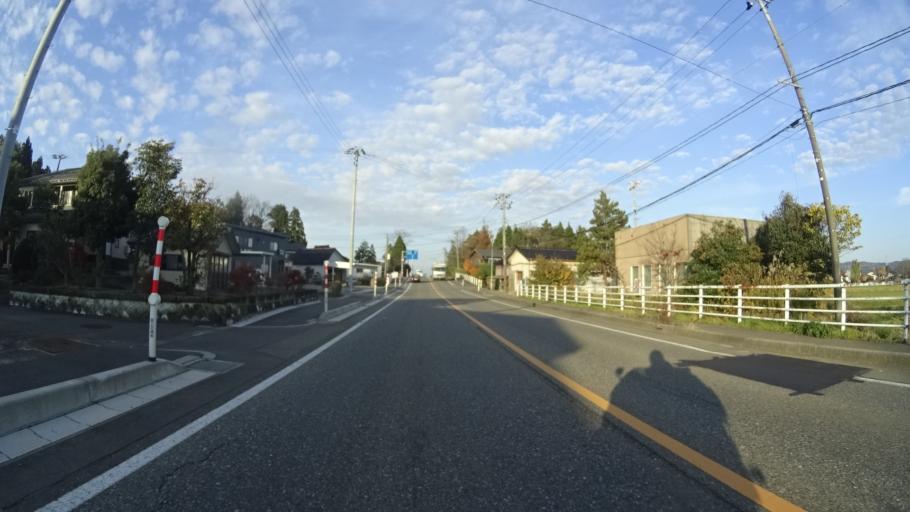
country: JP
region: Niigata
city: Kashiwazaki
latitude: 37.3948
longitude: 138.6026
